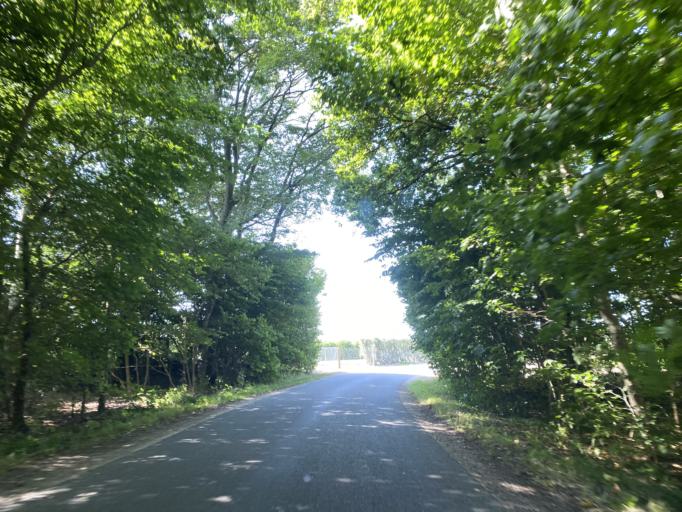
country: DK
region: Central Jutland
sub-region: Favrskov Kommune
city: Hammel
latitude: 56.2514
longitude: 9.8054
